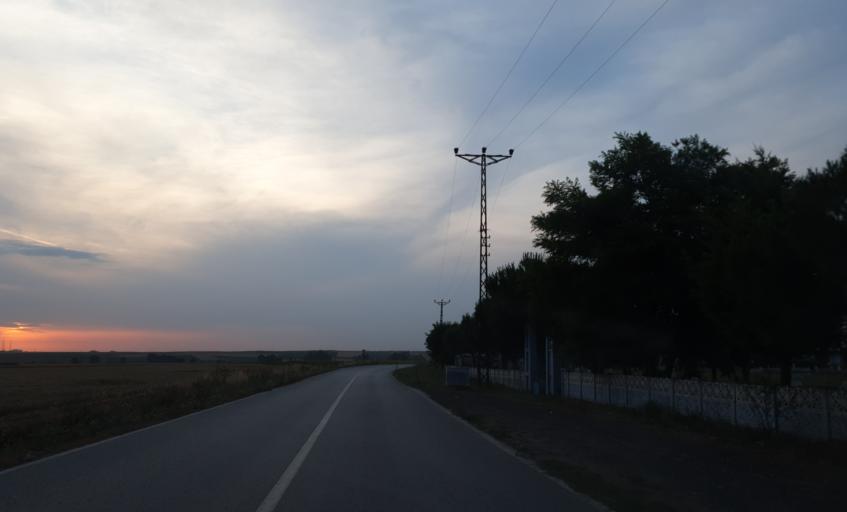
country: TR
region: Kirklareli
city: Buyukkaristiran
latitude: 41.3518
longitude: 27.6083
